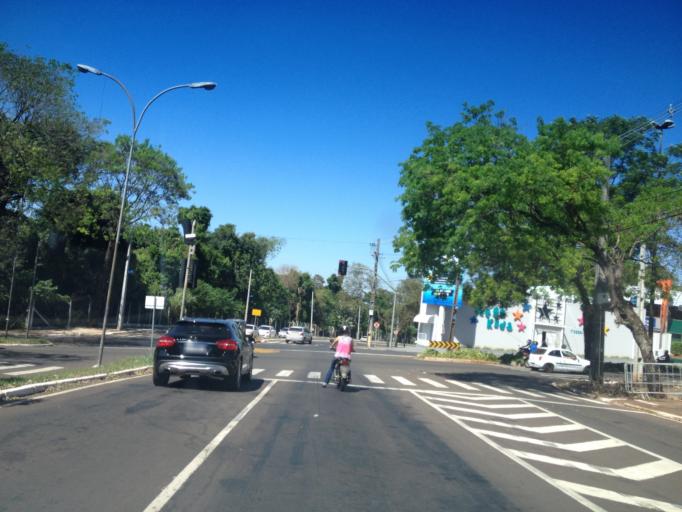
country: BR
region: Parana
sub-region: Maringa
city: Maringa
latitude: -23.4345
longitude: -51.9446
